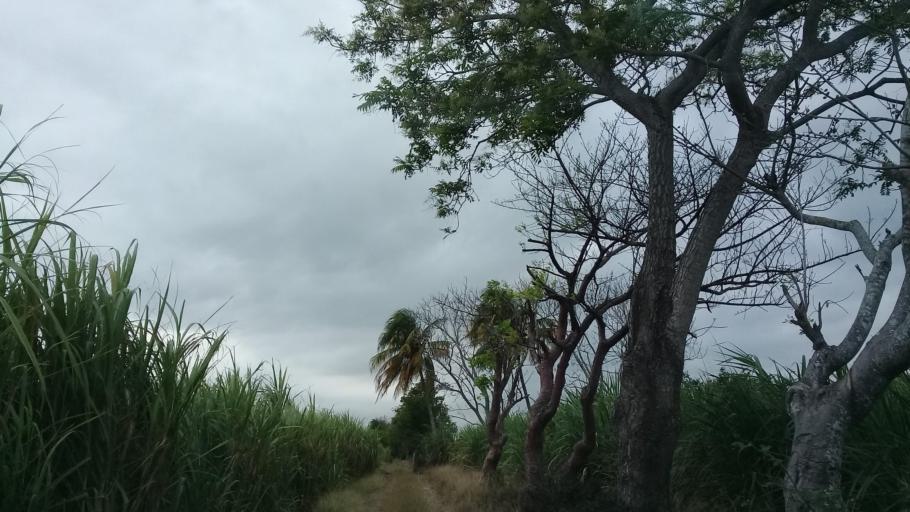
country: MX
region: Veracruz
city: Ursulo Galvan
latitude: 19.3829
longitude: -96.3578
